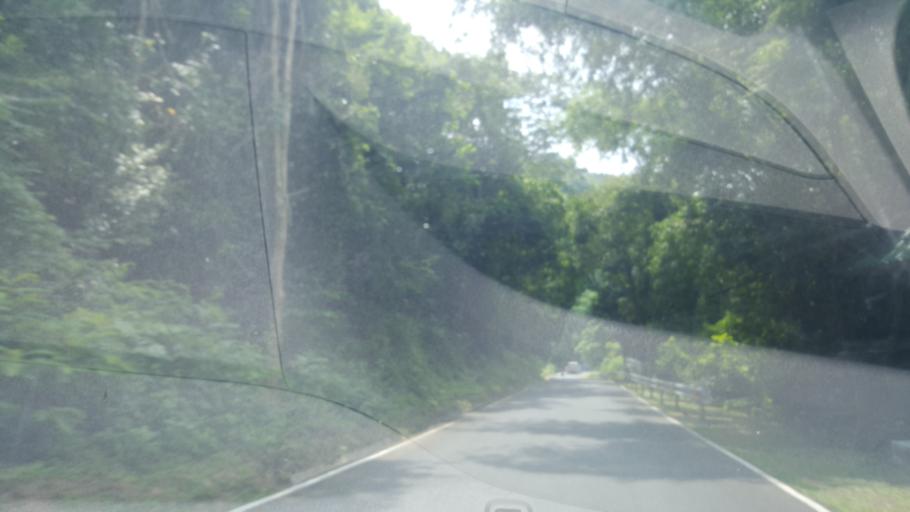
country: TH
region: Chon Buri
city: Ban Bueng
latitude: 13.2096
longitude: 101.0596
